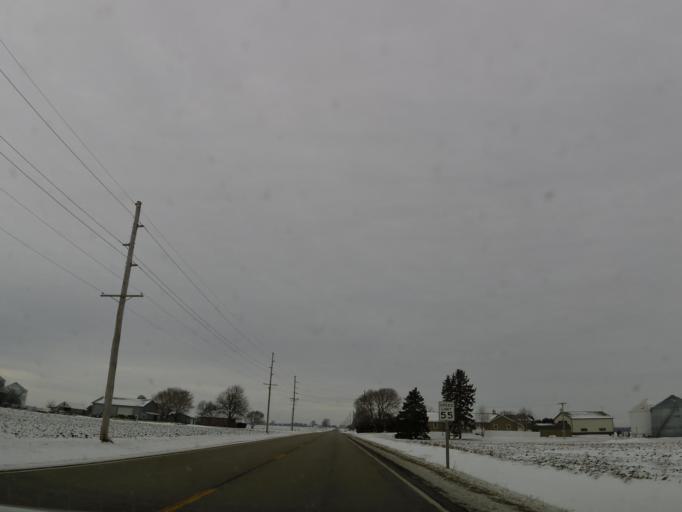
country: US
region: Illinois
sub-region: LaSalle County
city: Oglesby
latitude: 41.2650
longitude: -89.0890
